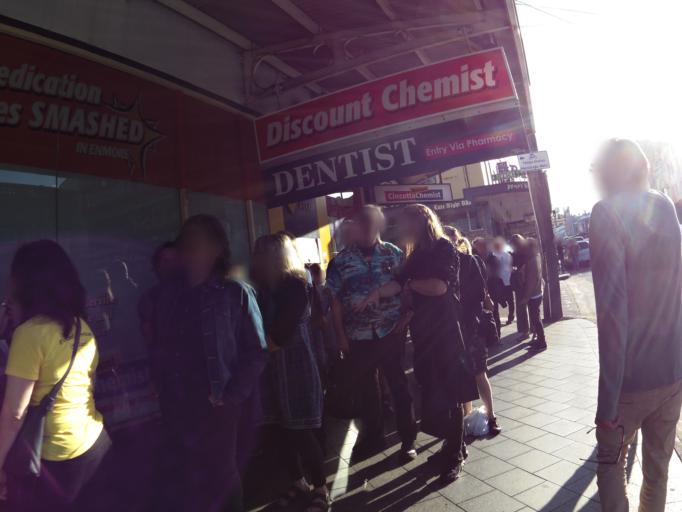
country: AU
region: New South Wales
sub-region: Marrickville
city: Newtown
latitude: -33.8989
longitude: 151.1739
